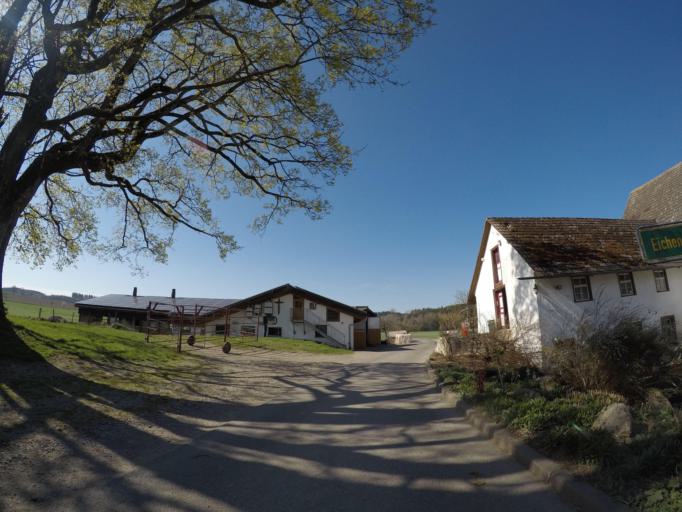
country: DE
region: Baden-Wuerttemberg
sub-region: Tuebingen Region
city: Fleischwangen
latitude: 47.8801
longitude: 9.4685
